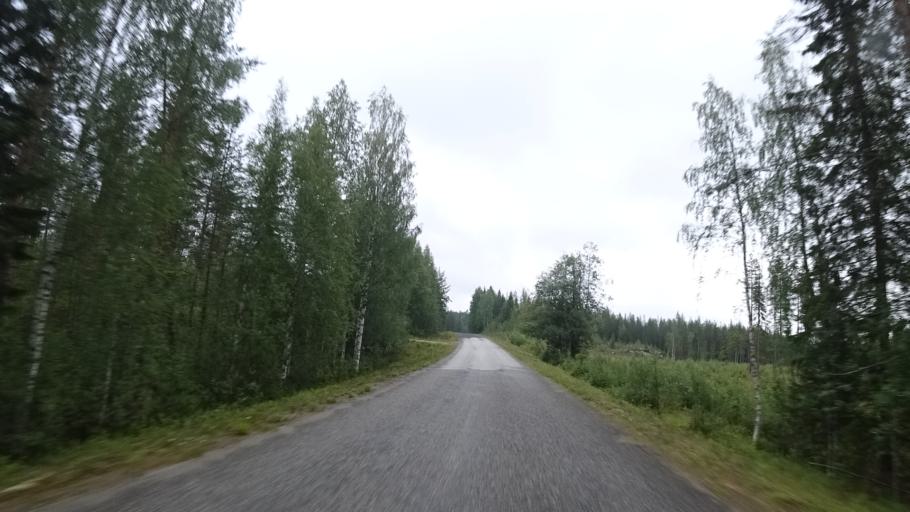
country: FI
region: North Karelia
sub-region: Joensuu
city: Ilomantsi
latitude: 63.2274
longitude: 30.8330
